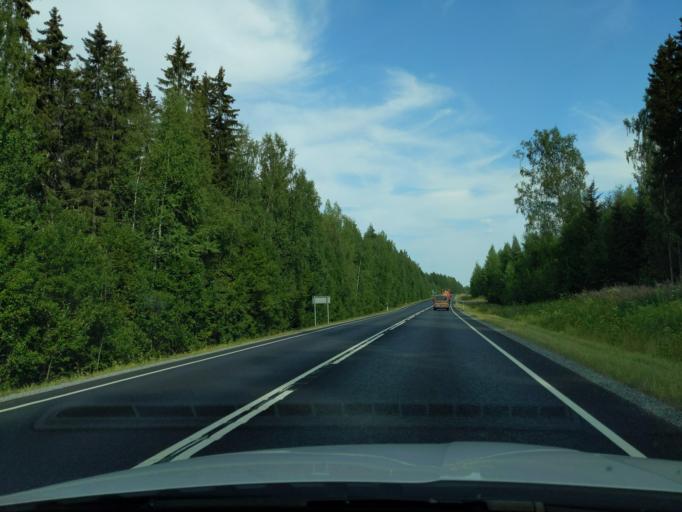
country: FI
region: Haeme
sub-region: Haemeenlinna
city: Hauho
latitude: 61.1731
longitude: 24.6029
